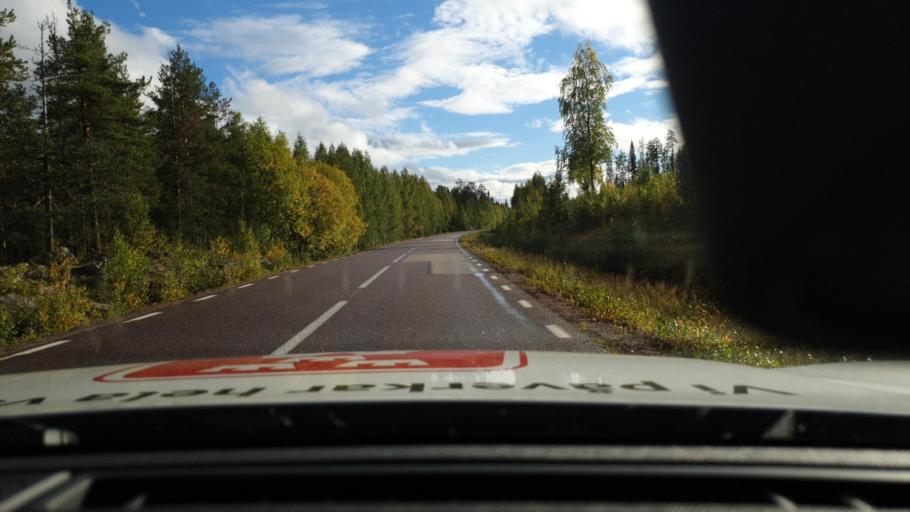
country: SE
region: Norrbotten
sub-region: Overkalix Kommun
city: OEverkalix
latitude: 66.8121
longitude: 22.7413
